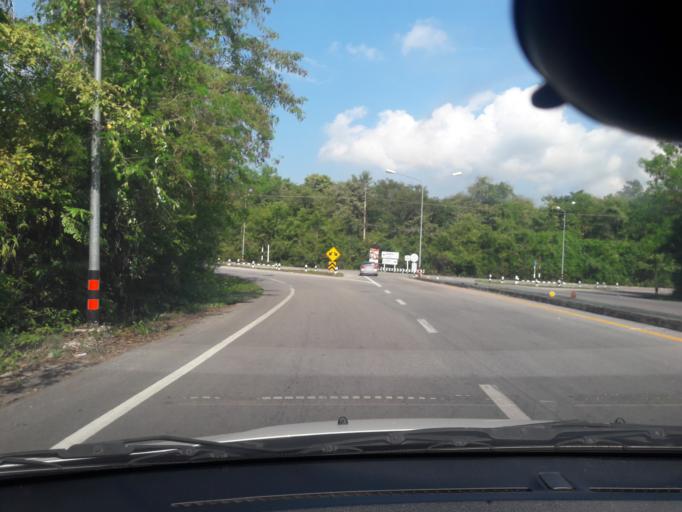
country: TH
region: Lampang
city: Mae Tha
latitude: 18.1874
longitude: 99.5479
